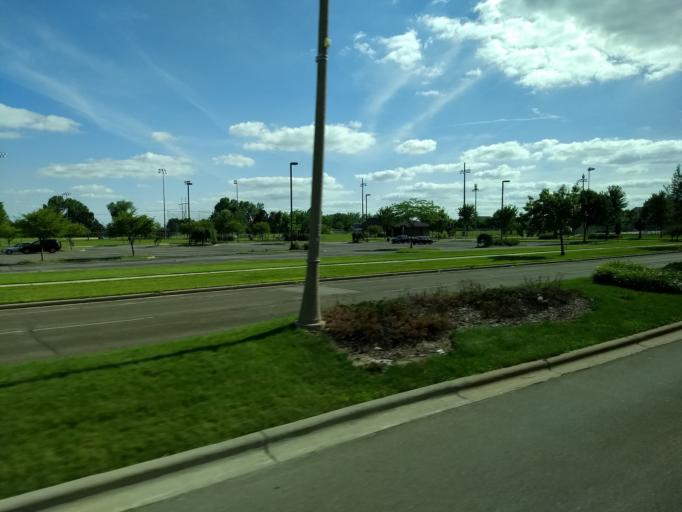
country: US
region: Wisconsin
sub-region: Dane County
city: Monona
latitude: 43.0482
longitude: -89.3179
